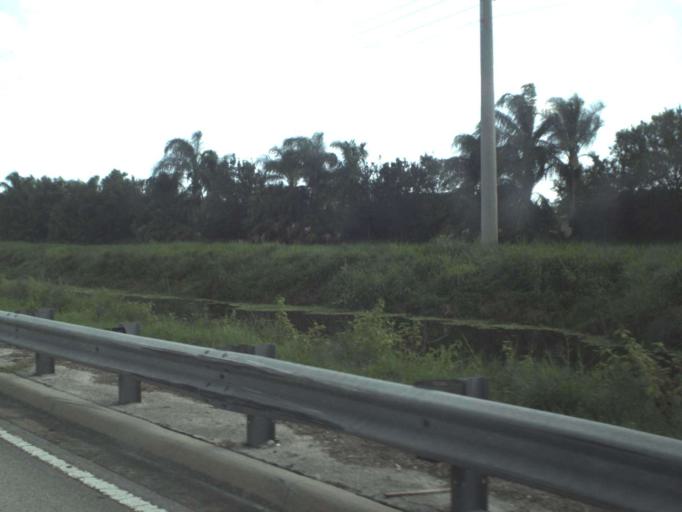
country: US
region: Florida
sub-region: Indian River County
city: Vero Beach South
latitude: 27.6256
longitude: -80.4469
